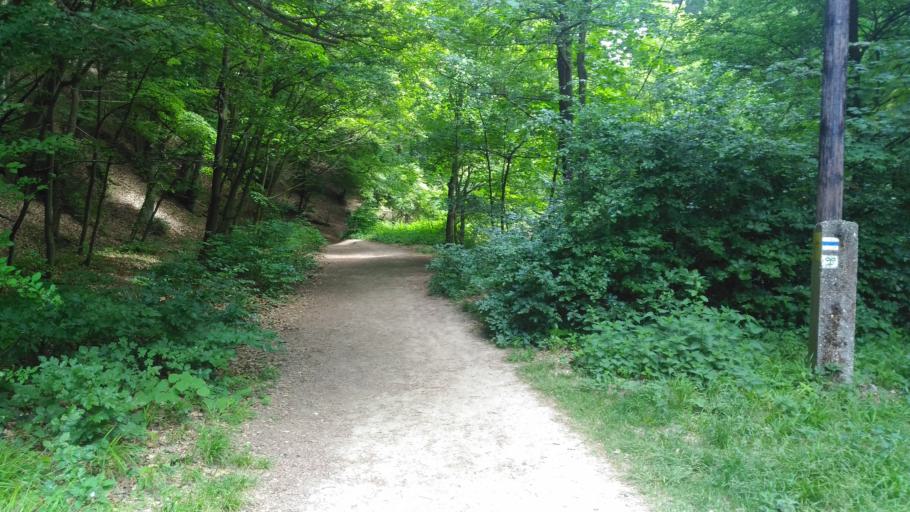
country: HU
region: Baranya
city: Szaszvar
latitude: 46.2188
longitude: 18.3977
